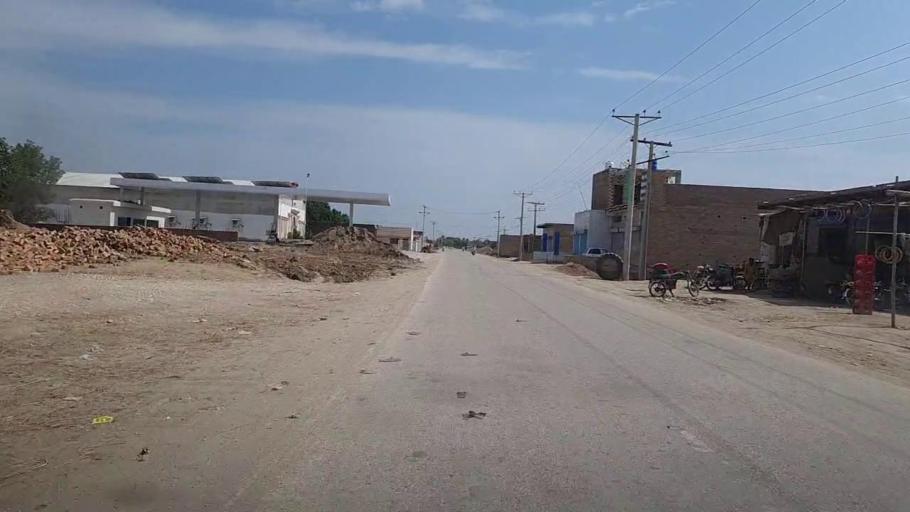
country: PK
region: Sindh
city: Thul
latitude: 28.2447
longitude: 68.7859
